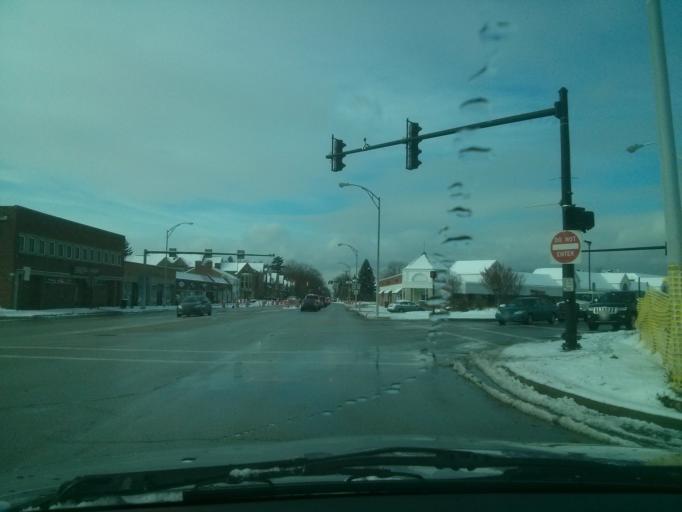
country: US
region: Ohio
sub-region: Cuyahoga County
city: Shaker Heights
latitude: 41.4646
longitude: -81.5364
